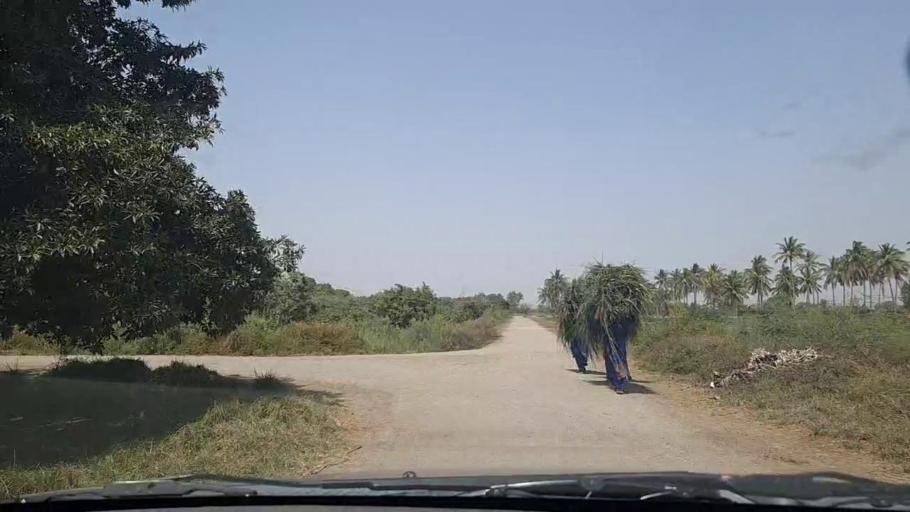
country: PK
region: Sindh
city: Keti Bandar
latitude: 24.2820
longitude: 67.6725
